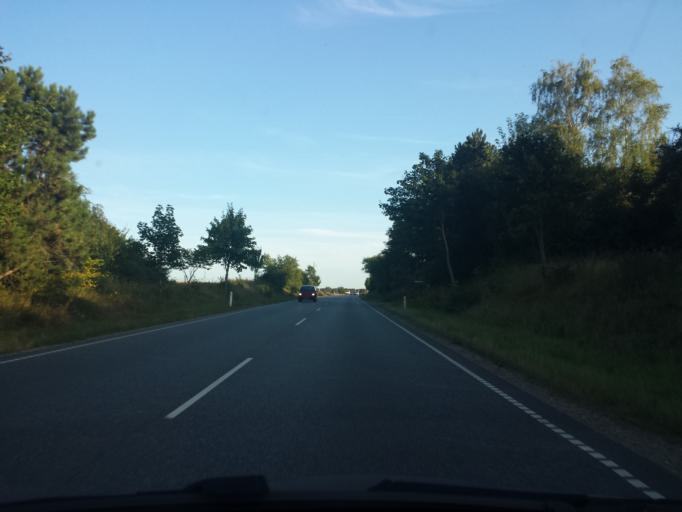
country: DK
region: Capital Region
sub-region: Frederikssund Kommune
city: Frederikssund
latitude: 55.8416
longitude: 12.0973
